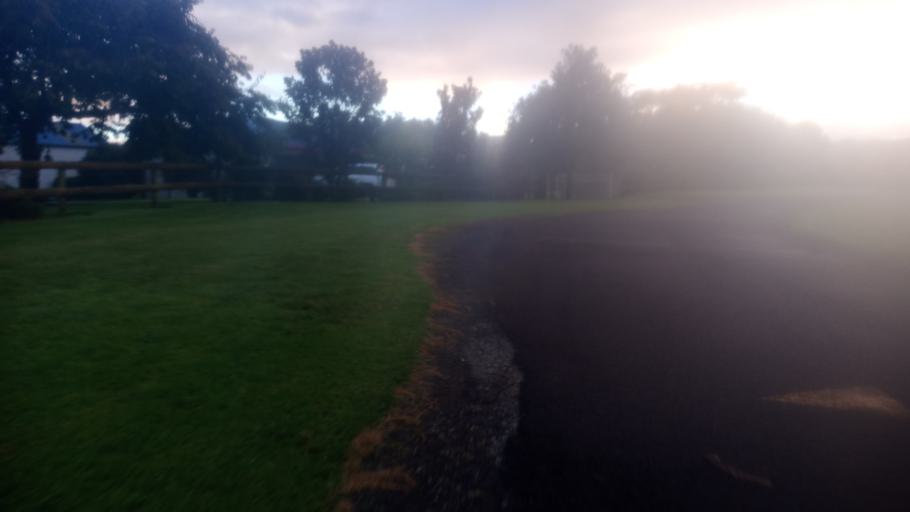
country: NZ
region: Gisborne
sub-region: Gisborne District
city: Gisborne
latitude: -38.6409
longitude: 177.9887
